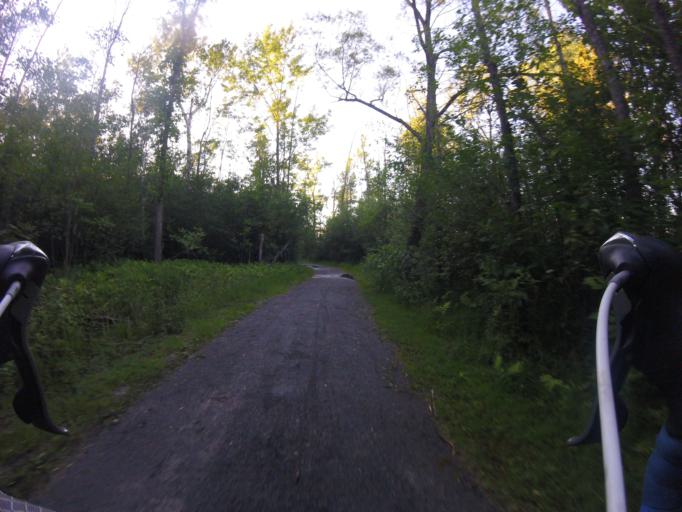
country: CA
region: Ontario
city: Bells Corners
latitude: 45.3616
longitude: -75.8744
